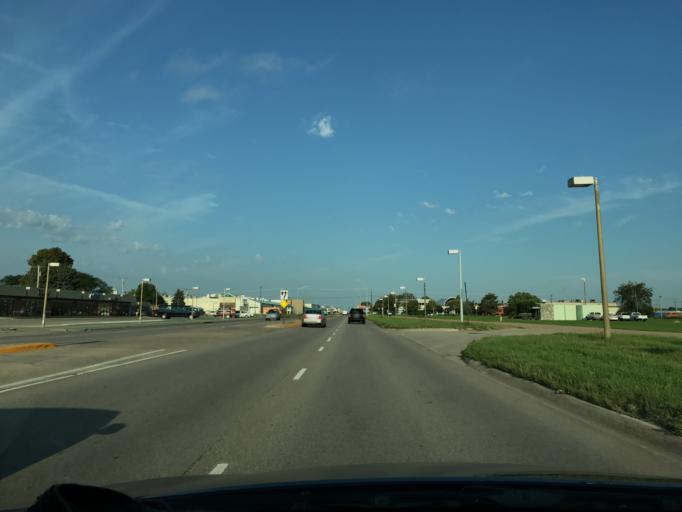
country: US
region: Nebraska
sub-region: Platte County
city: Columbus
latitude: 41.4385
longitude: -97.3363
